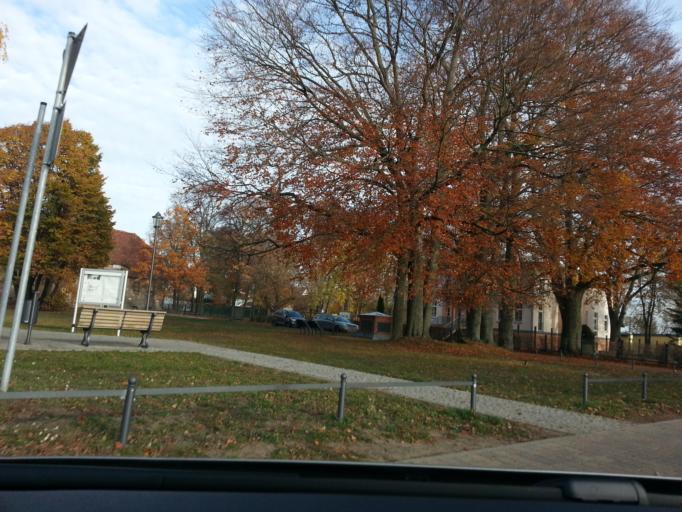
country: DE
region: Mecklenburg-Vorpommern
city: Torgelow
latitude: 53.6326
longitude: 14.0171
